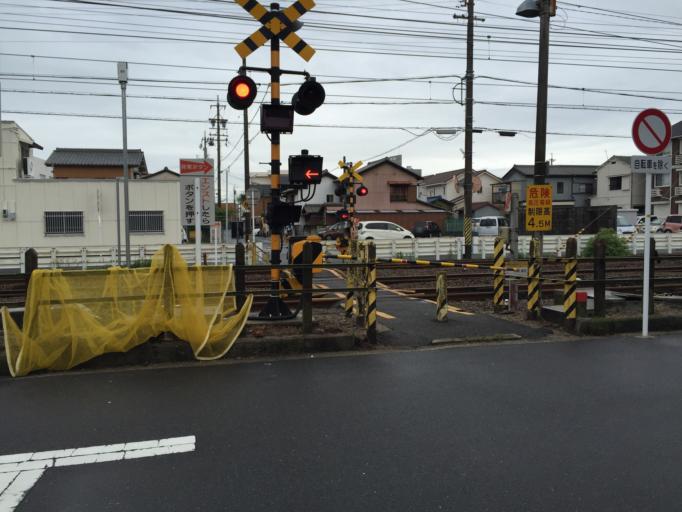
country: JP
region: Mie
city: Yokkaichi
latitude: 34.9663
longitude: 136.6320
